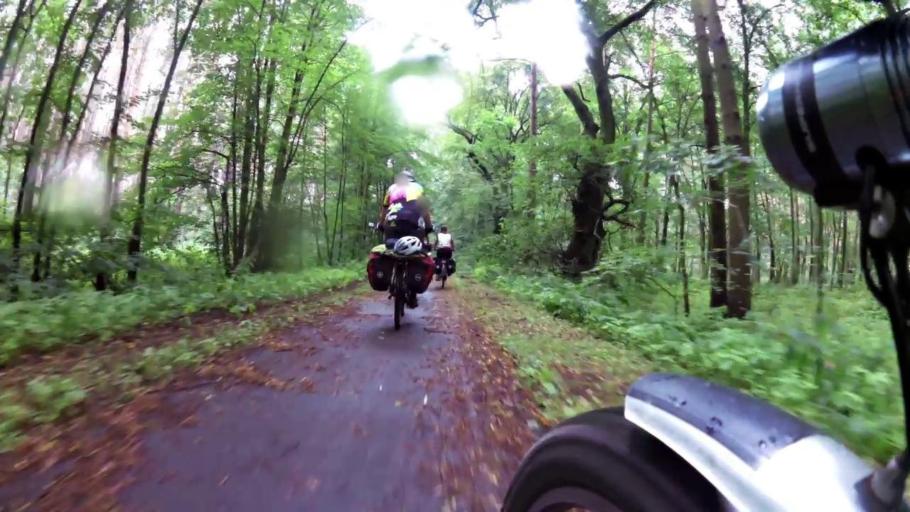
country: PL
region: West Pomeranian Voivodeship
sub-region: Powiat gryfinski
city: Banie
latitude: 53.0754
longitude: 14.6349
